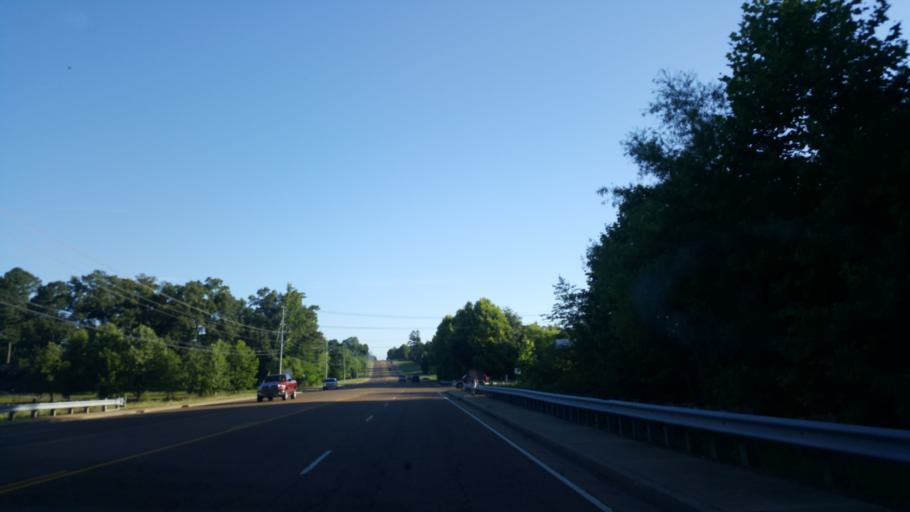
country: US
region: Tennessee
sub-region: Henderson County
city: Lexington
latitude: 35.6676
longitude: -88.3843
